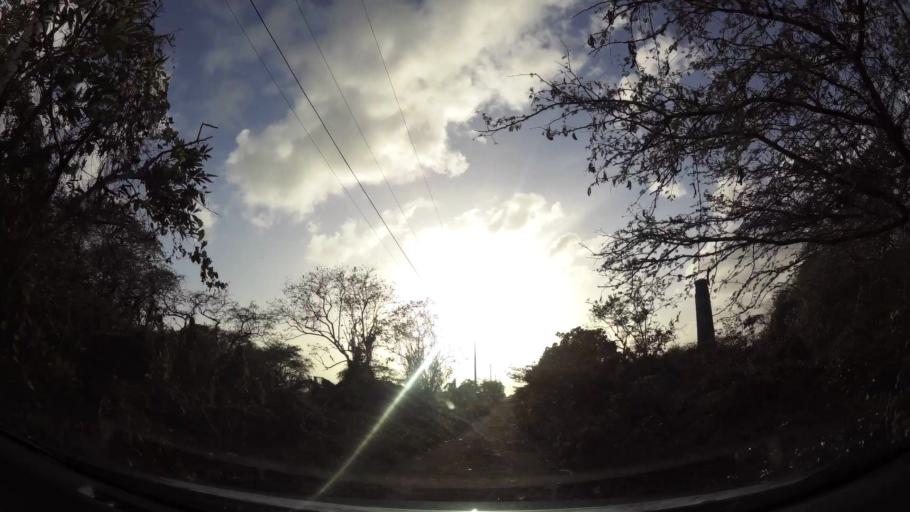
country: KN
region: Saint John Figtree
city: Fig Tree
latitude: 17.1181
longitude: -62.6106
